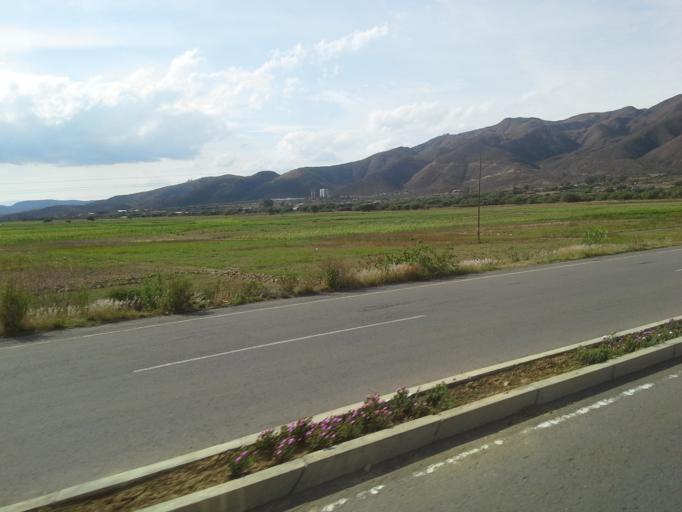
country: BO
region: Cochabamba
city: Tarata
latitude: -17.5515
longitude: -66.0069
